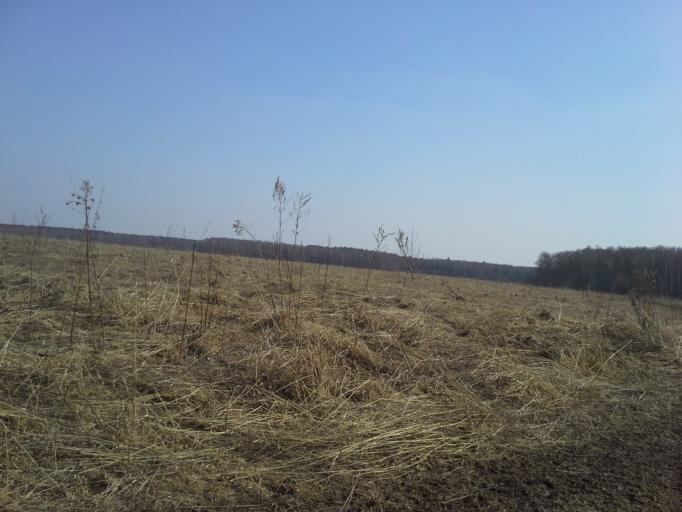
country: RU
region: Moskovskaya
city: Filimonki
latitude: 55.5558
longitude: 37.3944
